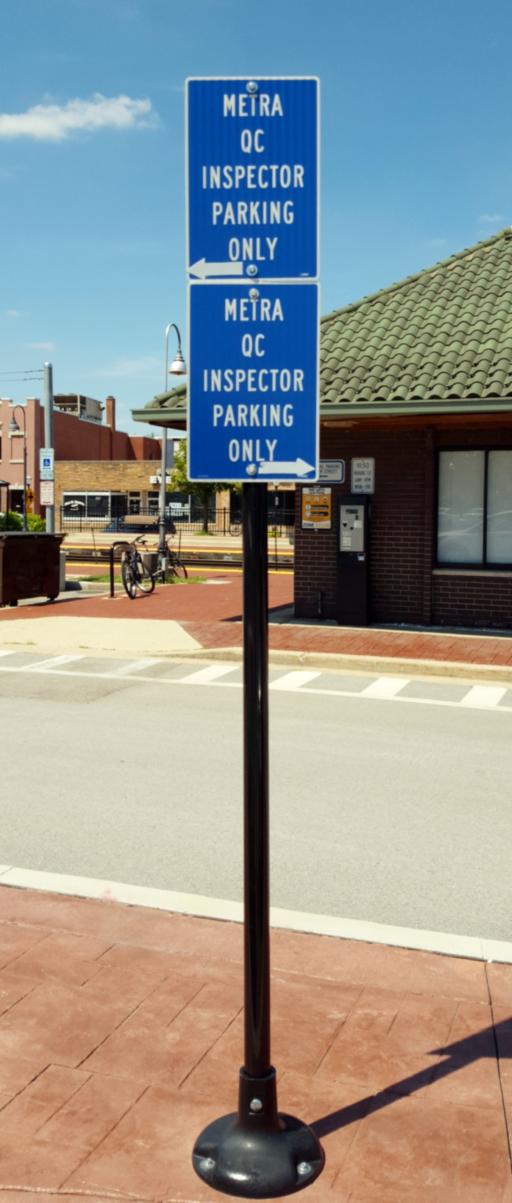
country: US
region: Illinois
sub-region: DuPage County
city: Bensenville
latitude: 41.9567
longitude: -87.9420
